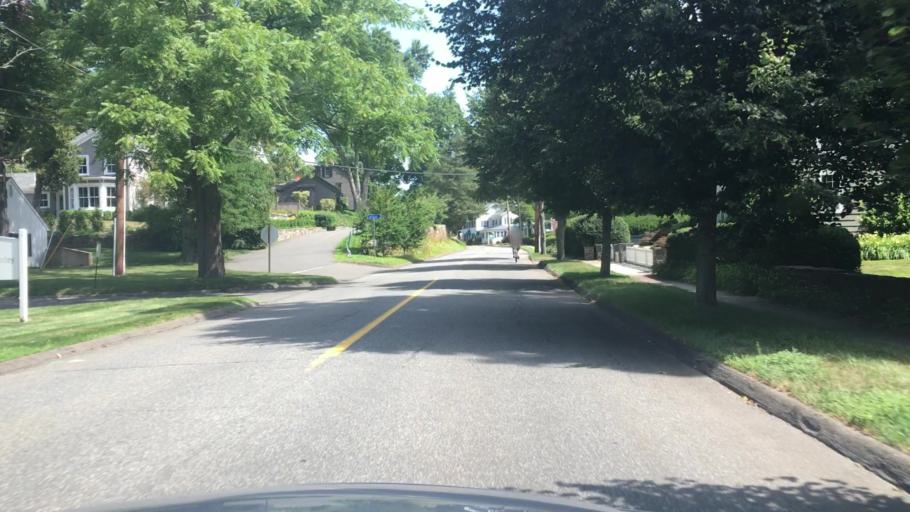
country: US
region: Connecticut
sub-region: Middlesex County
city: Essex Village
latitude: 41.3470
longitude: -72.3940
